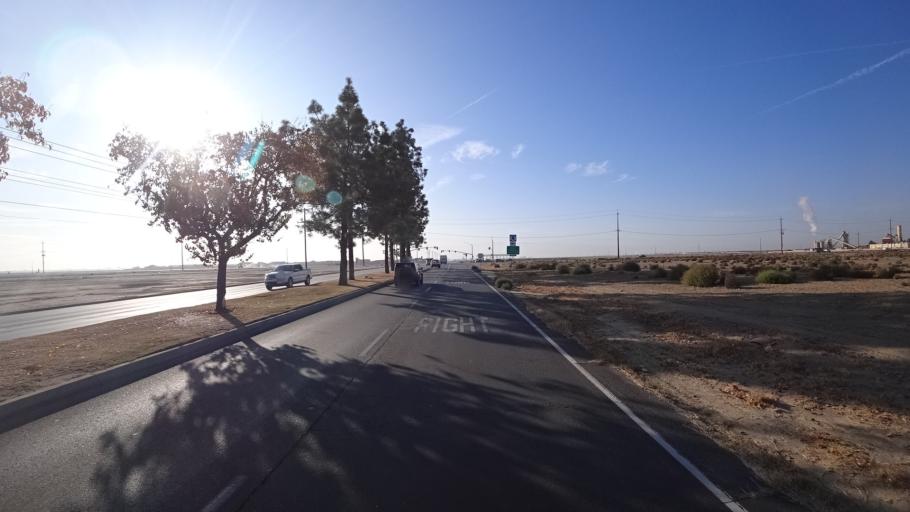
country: US
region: California
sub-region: Kern County
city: Greenacres
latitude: 35.2979
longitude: -119.0923
